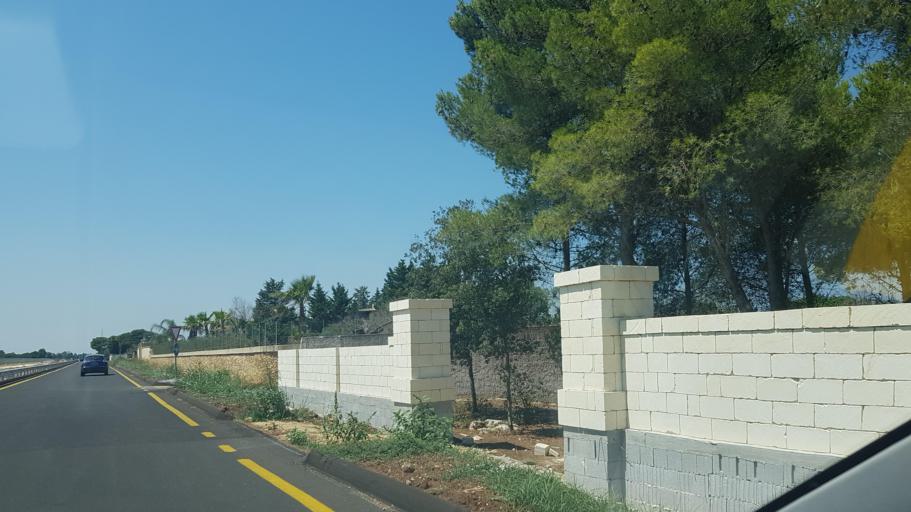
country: IT
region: Apulia
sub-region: Provincia di Lecce
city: Struda
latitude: 40.3264
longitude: 18.2563
